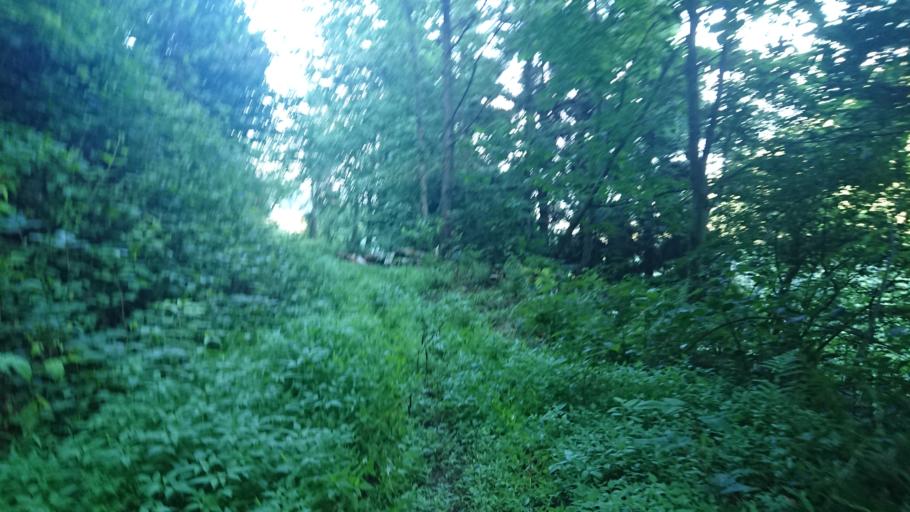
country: TR
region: Rize
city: Rize
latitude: 40.9727
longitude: 40.4958
